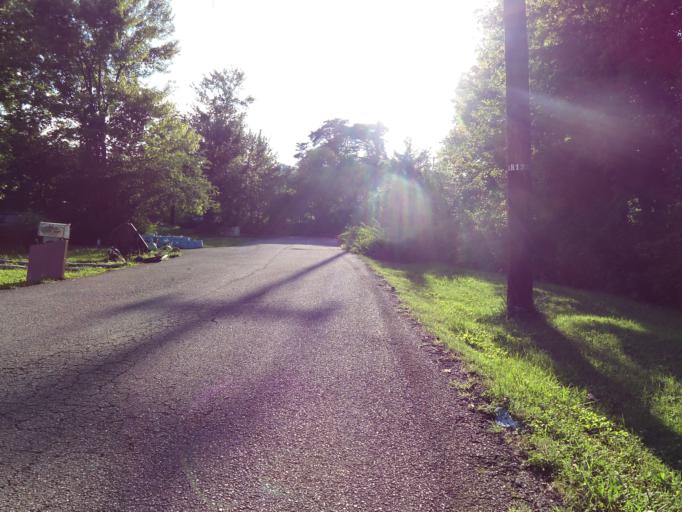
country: US
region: Tennessee
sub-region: Knox County
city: Knoxville
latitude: 36.0075
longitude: -83.9289
